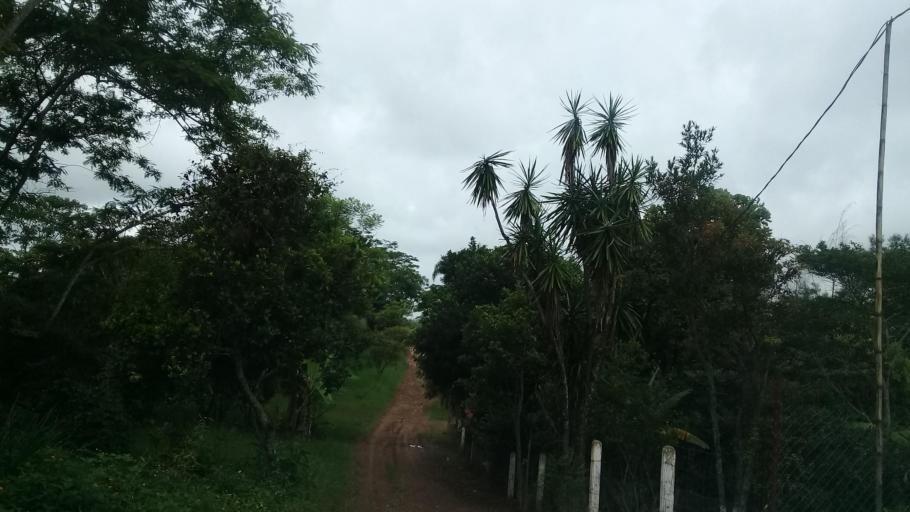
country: MX
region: Veracruz
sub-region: Emiliano Zapata
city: Jacarandas
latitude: 19.4844
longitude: -96.8554
